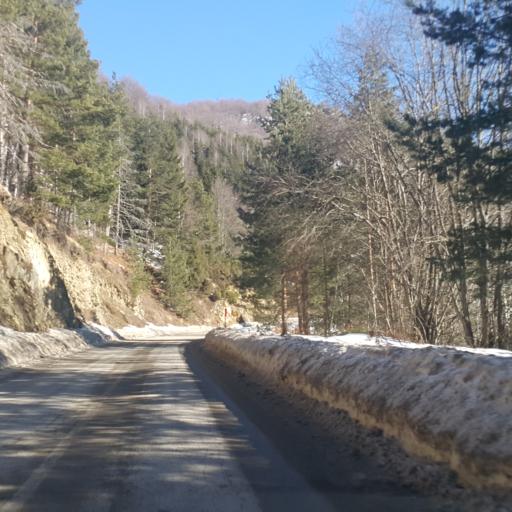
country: XK
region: Mitrovica
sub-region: Komuna e Leposaviqit
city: Leposaviq
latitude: 43.3099
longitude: 20.8632
